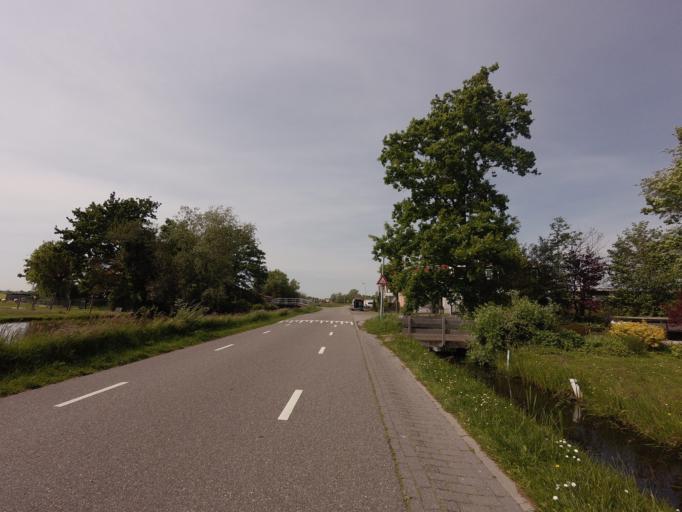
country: NL
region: North Holland
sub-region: Gemeente Uitgeest
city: Uitgeest
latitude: 52.5099
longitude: 4.7699
